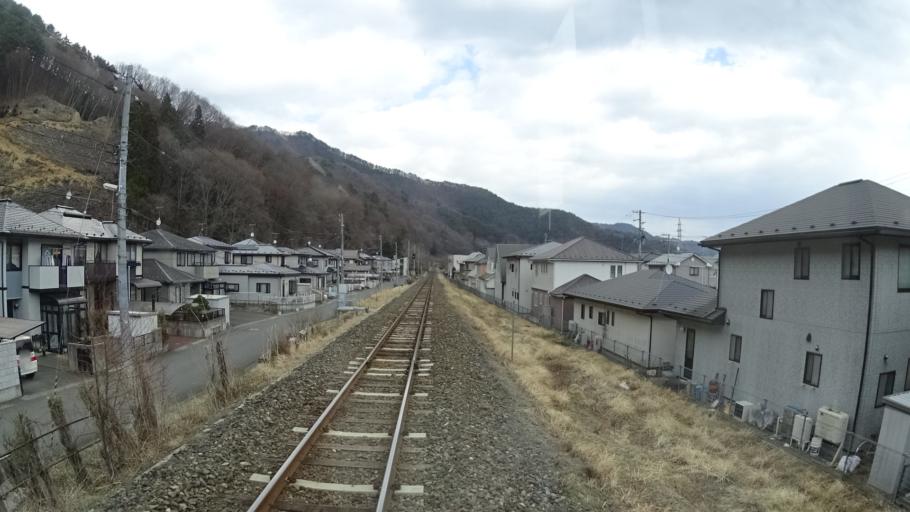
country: JP
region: Iwate
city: Kamaishi
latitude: 39.2731
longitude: 141.8599
